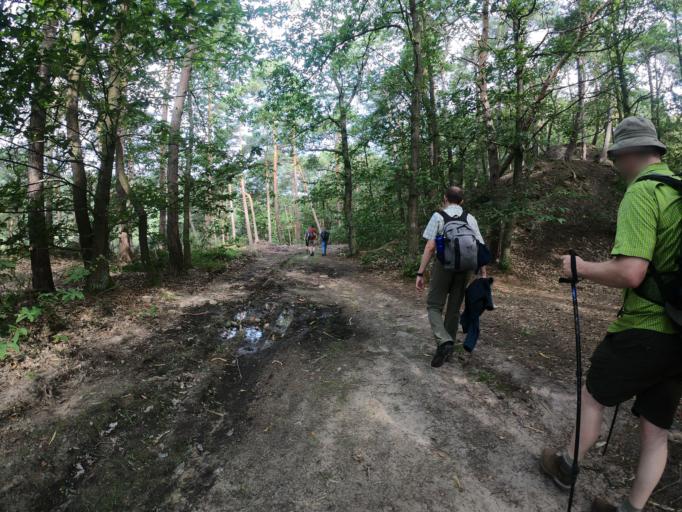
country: DE
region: Rheinland-Pfalz
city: Gleiszellen-Gleishorbach
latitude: 49.1306
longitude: 7.9943
